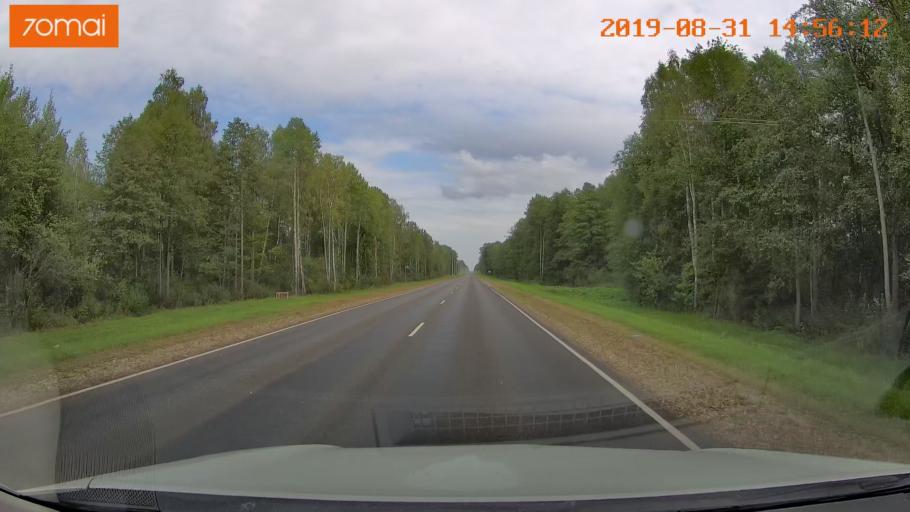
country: RU
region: Kaluga
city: Spas-Demensk
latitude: 54.3034
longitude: 33.9331
